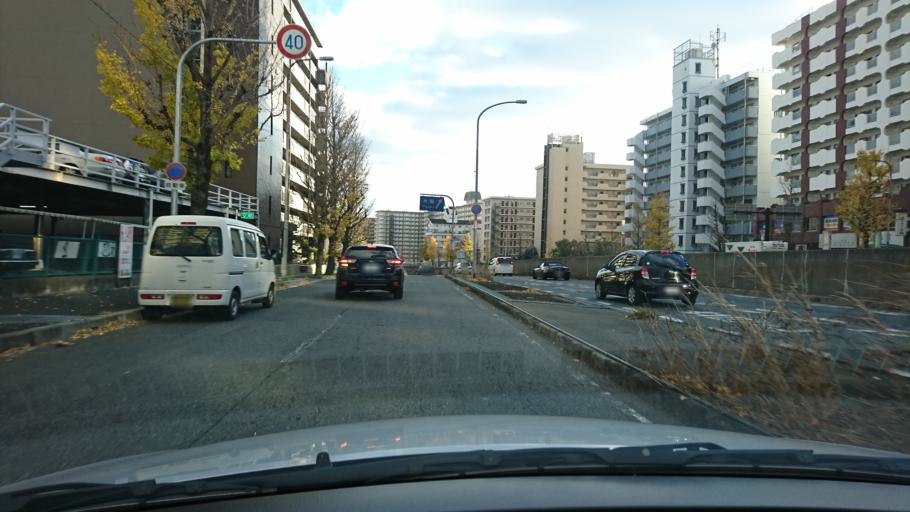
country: JP
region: Osaka
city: Suita
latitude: 34.7750
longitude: 135.4955
